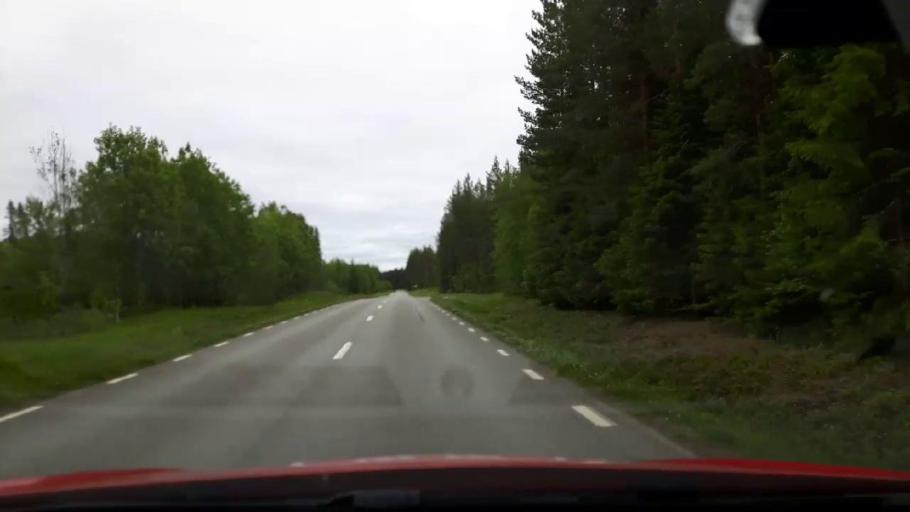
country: SE
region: Jaemtland
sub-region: Stroemsunds Kommun
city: Stroemsund
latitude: 63.4393
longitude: 15.4855
